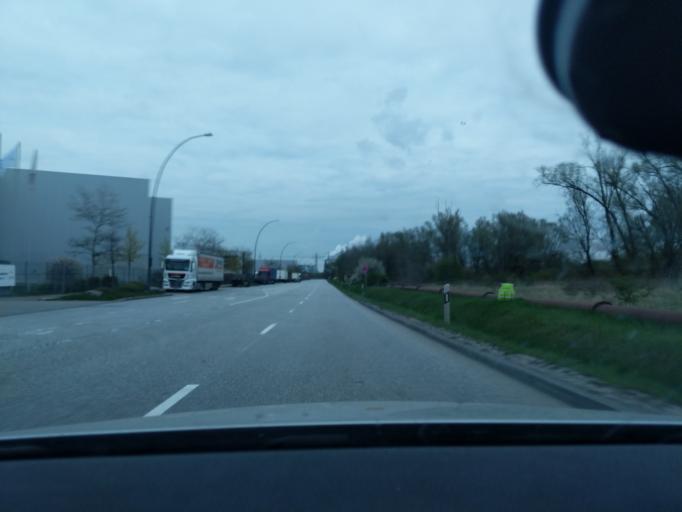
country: DE
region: Hamburg
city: Altona
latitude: 53.5050
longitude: 9.8962
